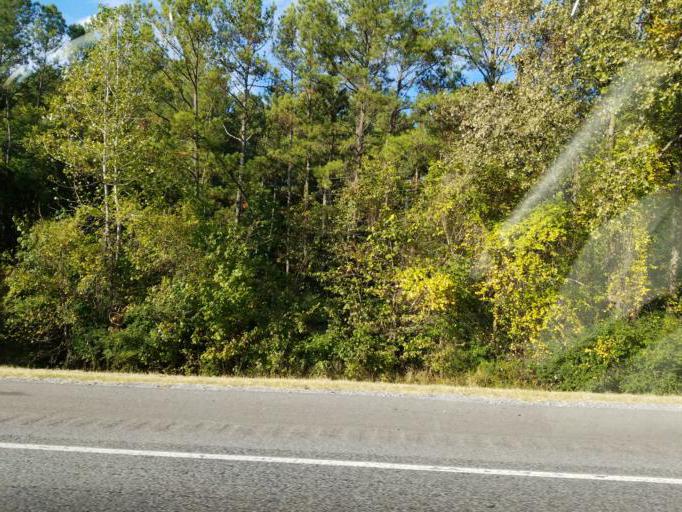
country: US
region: Georgia
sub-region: Cobb County
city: Acworth
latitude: 34.0884
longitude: -84.7188
